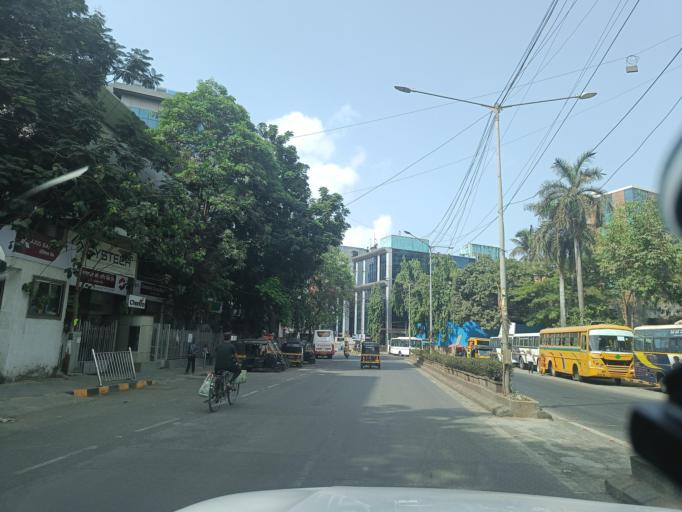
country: IN
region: Maharashtra
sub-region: Mumbai Suburban
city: Powai
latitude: 19.1225
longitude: 72.8710
